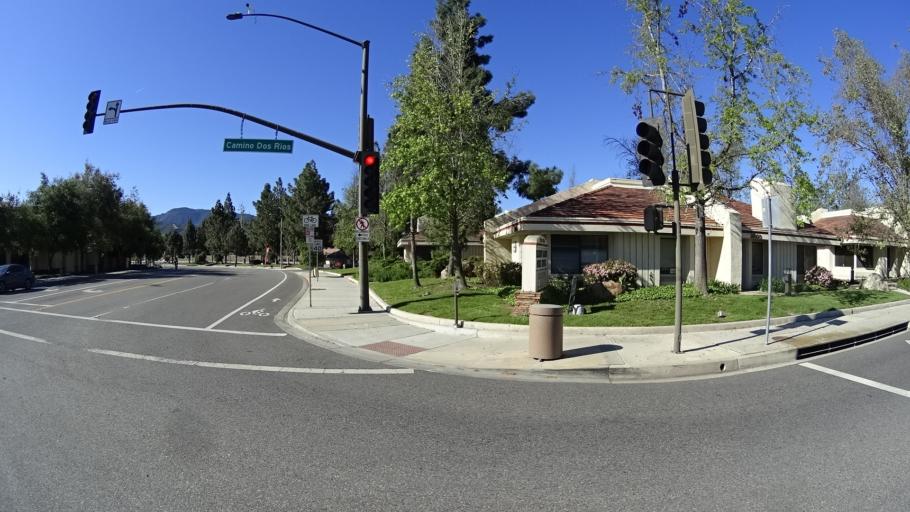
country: US
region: California
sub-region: Ventura County
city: Casa Conejo
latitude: 34.1900
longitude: -118.9352
